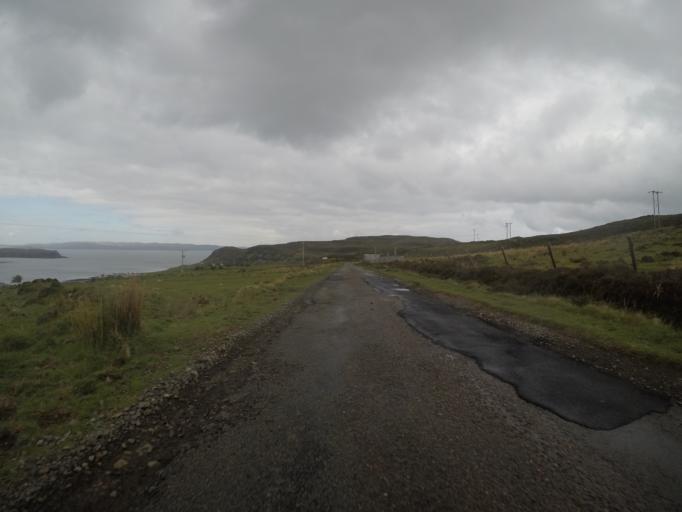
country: GB
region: Scotland
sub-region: Highland
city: Portree
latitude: 57.5941
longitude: -6.3653
